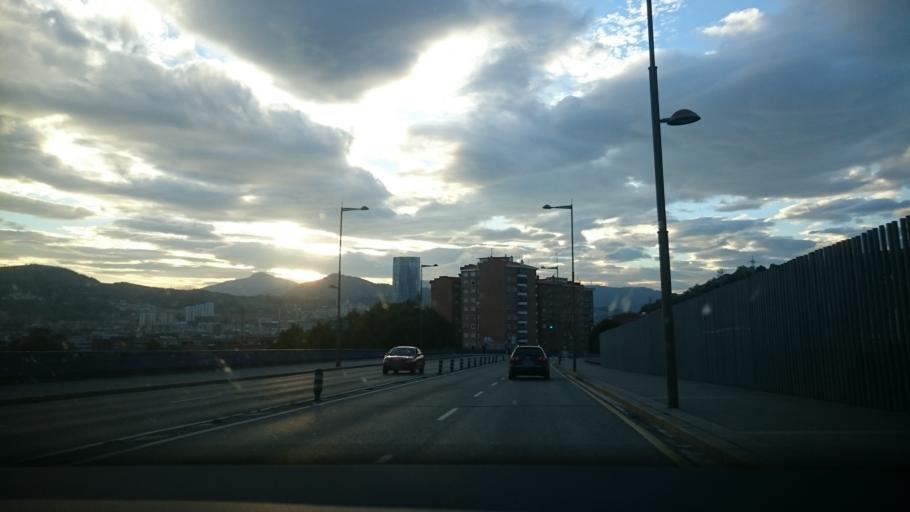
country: ES
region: Basque Country
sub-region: Bizkaia
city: Bilbao
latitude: 43.2699
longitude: -2.9238
